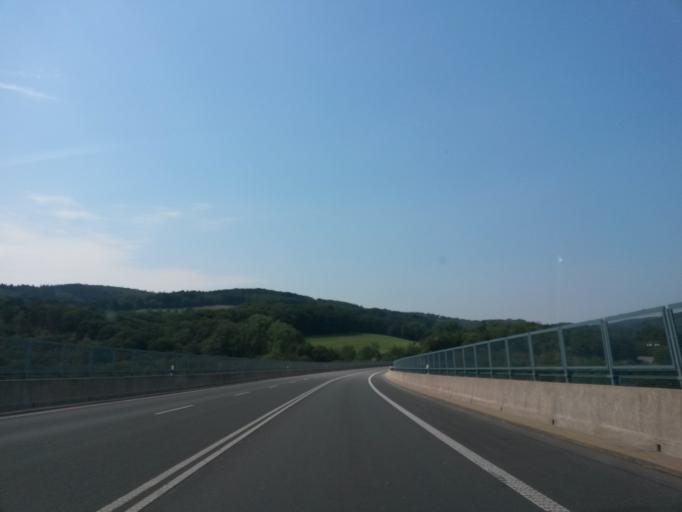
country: DE
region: North Rhine-Westphalia
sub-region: Regierungsbezirk Arnsberg
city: Hagen
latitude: 51.3416
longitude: 7.5105
